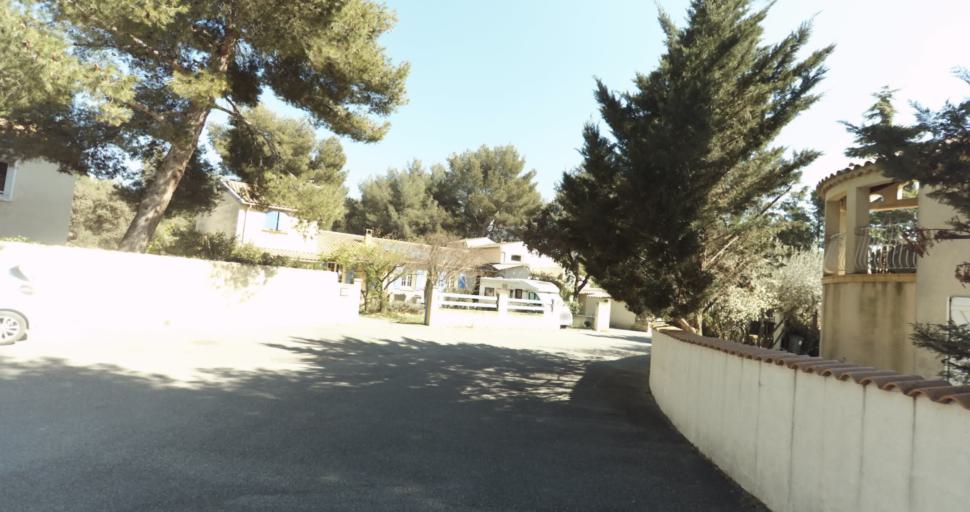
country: FR
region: Provence-Alpes-Cote d'Azur
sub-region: Departement des Bouches-du-Rhone
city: Pelissanne
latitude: 43.6383
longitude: 5.1604
